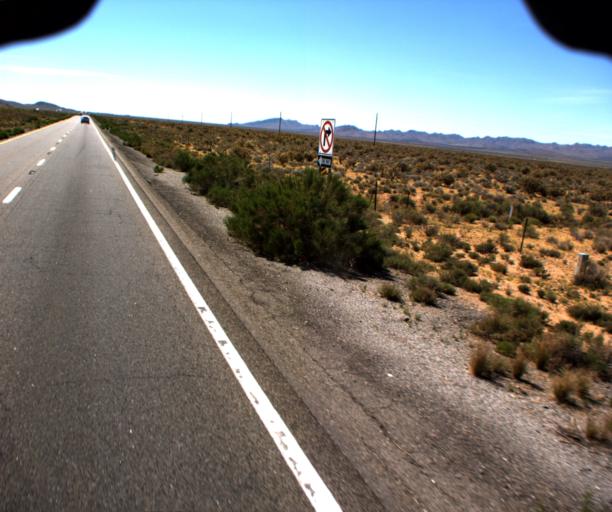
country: US
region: Arizona
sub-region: Mohave County
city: Dolan Springs
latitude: 35.4878
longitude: -114.3238
